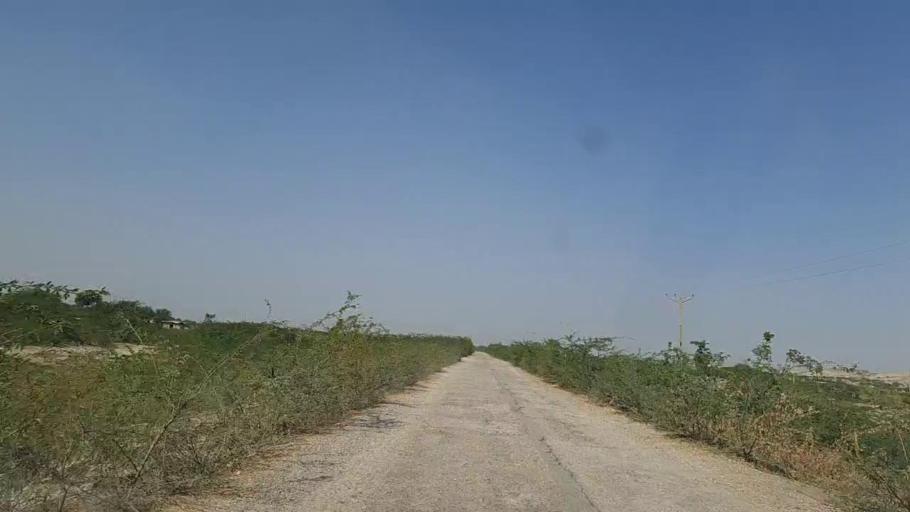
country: PK
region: Sindh
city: Naukot
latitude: 24.6334
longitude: 69.2883
